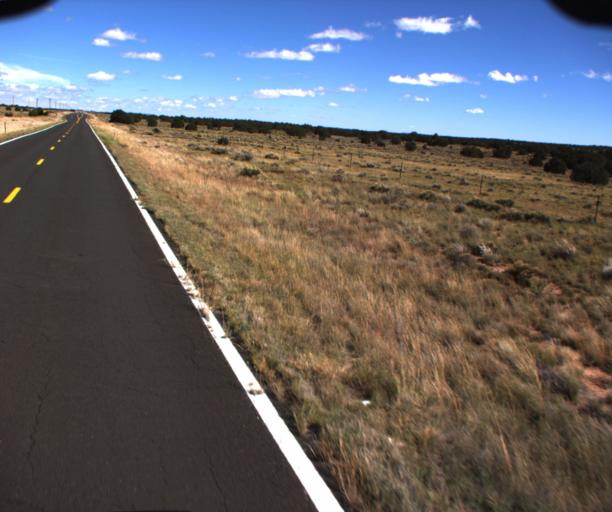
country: US
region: New Mexico
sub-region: McKinley County
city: Zuni Pueblo
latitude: 34.9623
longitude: -109.1545
